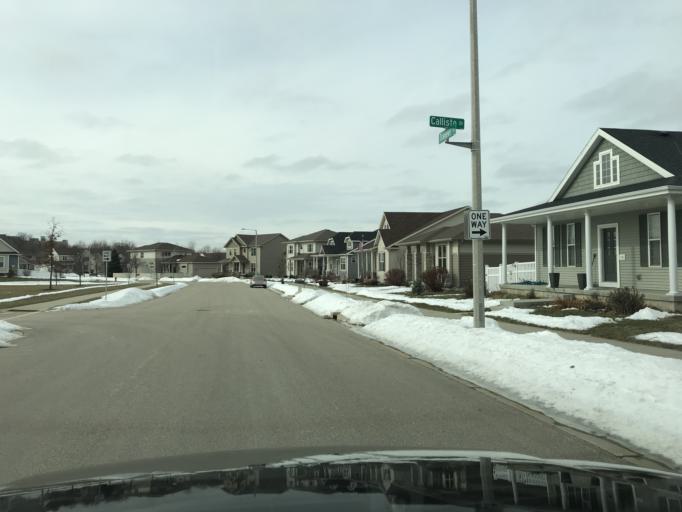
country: US
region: Wisconsin
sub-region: Dane County
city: Monona
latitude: 43.0888
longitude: -89.2720
